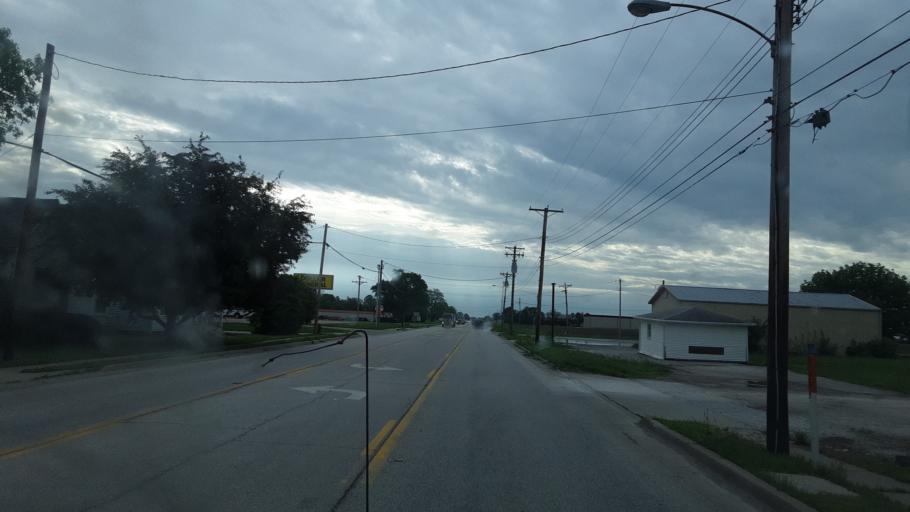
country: US
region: Illinois
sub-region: Hancock County
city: Hamilton
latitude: 40.3963
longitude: -91.3268
